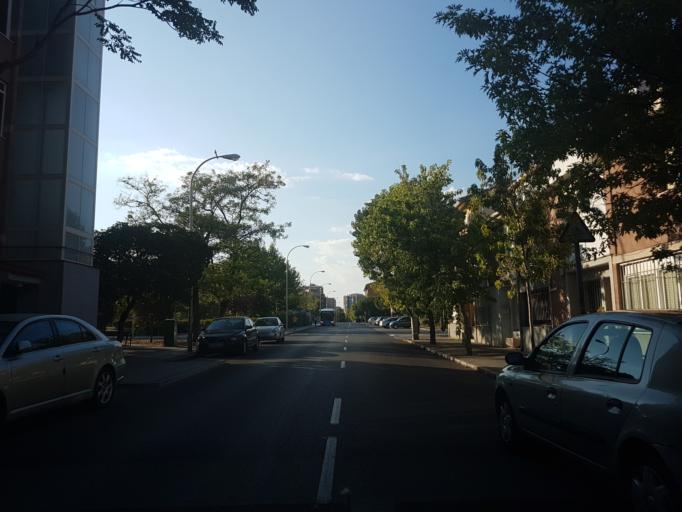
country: ES
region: Madrid
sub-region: Provincia de Madrid
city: Pinar de Chamartin
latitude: 40.4758
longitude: -3.6616
